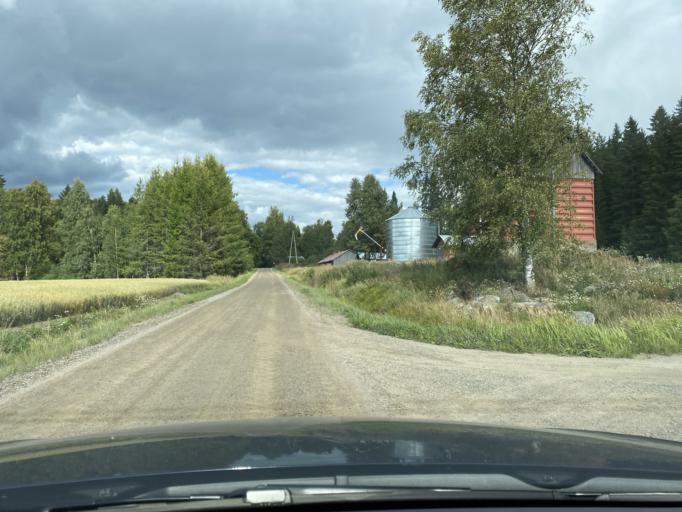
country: FI
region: Haeme
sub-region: Forssa
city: Humppila
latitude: 61.0736
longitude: 23.2732
